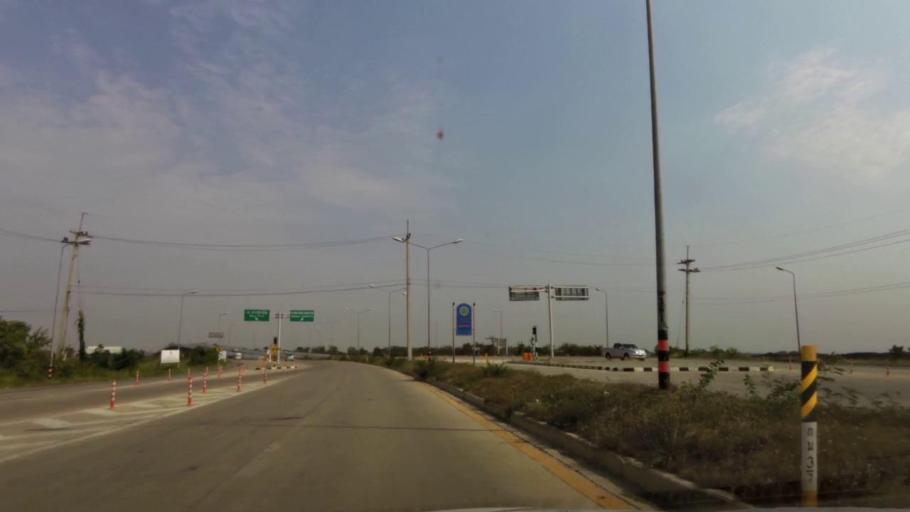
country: TH
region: Phra Nakhon Si Ayutthaya
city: Phra Nakhon Si Ayutthaya
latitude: 14.3304
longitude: 100.5788
